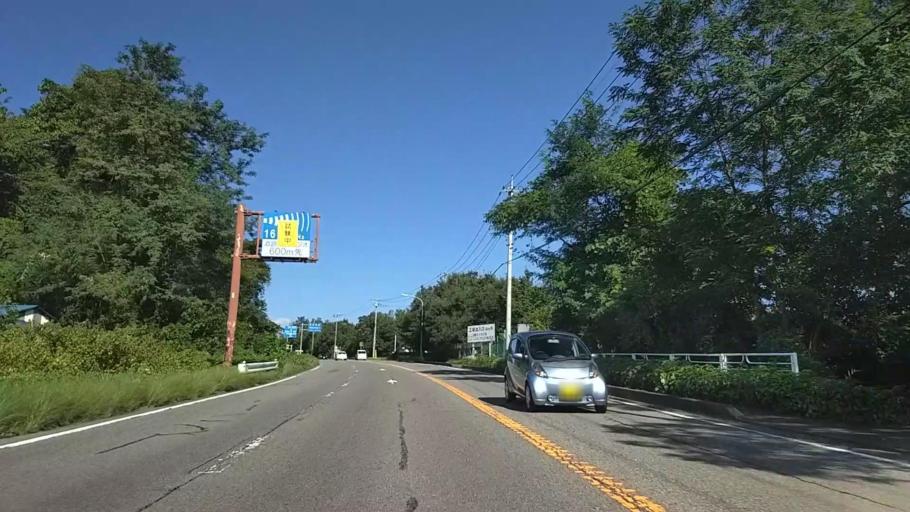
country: JP
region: Gunma
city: Annaka
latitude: 36.3119
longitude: 138.8128
